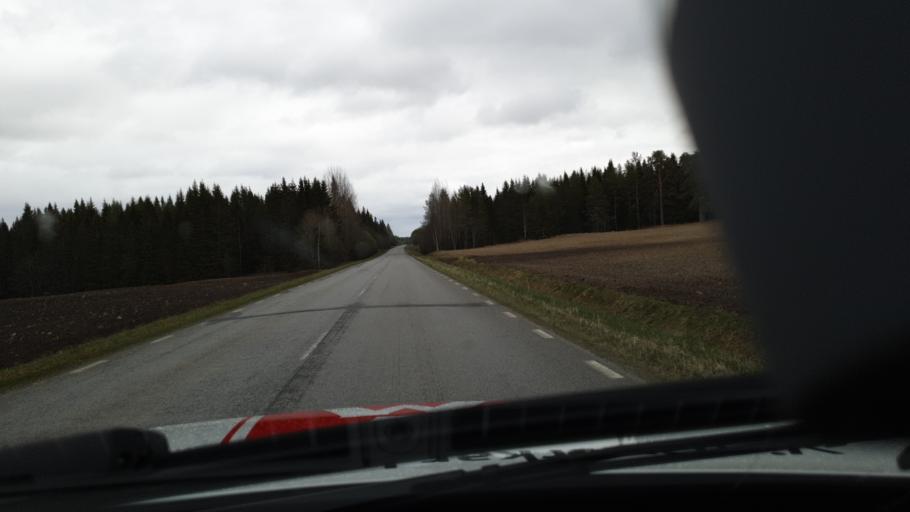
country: SE
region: Jaemtland
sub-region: Stroemsunds Kommun
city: Stroemsund
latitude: 63.6208
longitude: 15.2578
